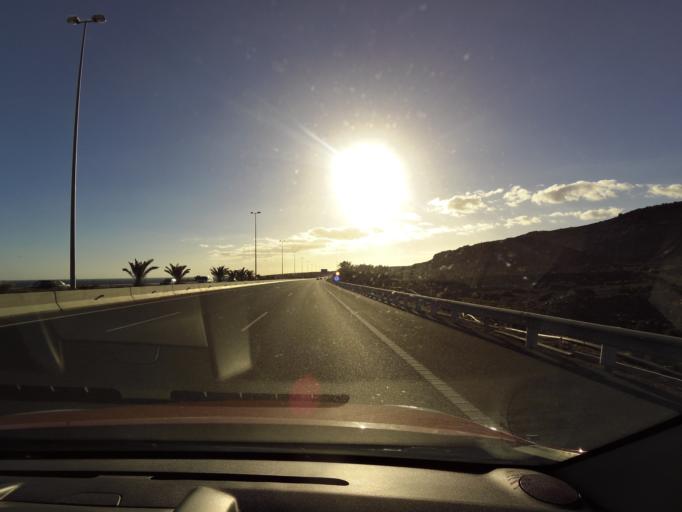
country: ES
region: Canary Islands
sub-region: Provincia de Las Palmas
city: Playa del Ingles
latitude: 27.7951
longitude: -15.4923
